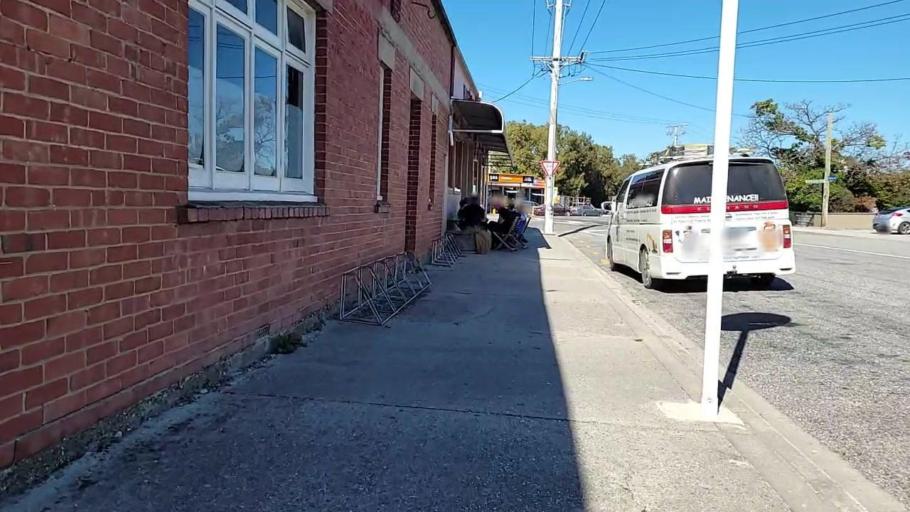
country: NZ
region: Otago
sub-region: Queenstown-Lakes District
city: Wanaka
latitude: -45.0938
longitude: 169.6020
